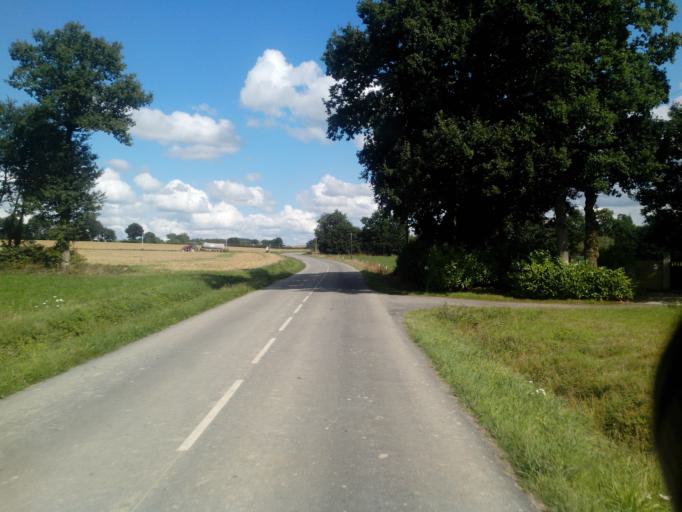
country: FR
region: Brittany
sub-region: Departement d'Ille-et-Vilaine
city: Gael
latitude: 48.1305
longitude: -2.2094
